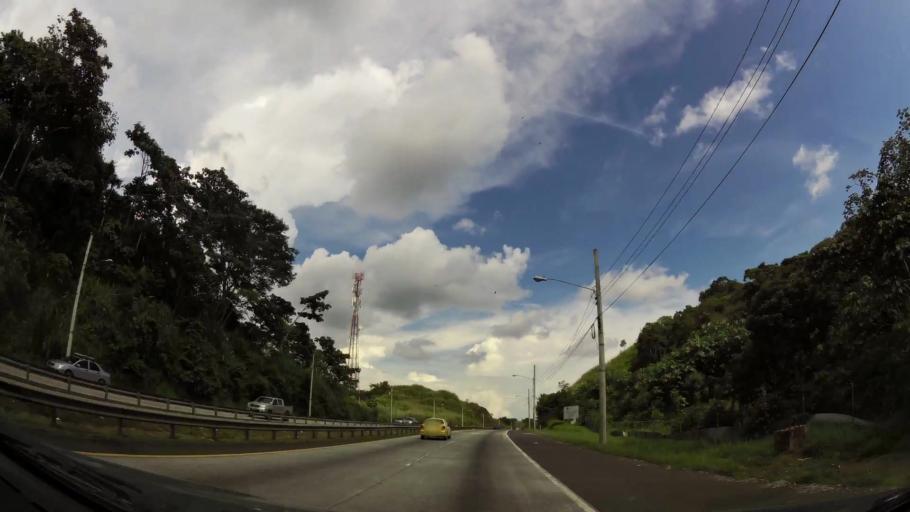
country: PA
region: Panama
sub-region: Distrito de Panama
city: Paraiso
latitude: 9.0411
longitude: -79.5673
